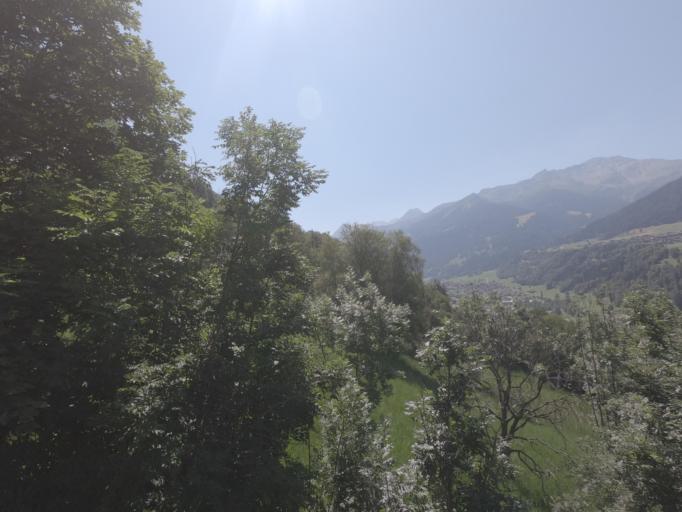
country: CH
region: Valais
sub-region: Entremont District
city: Bagnes
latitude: 46.0821
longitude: 7.2191
